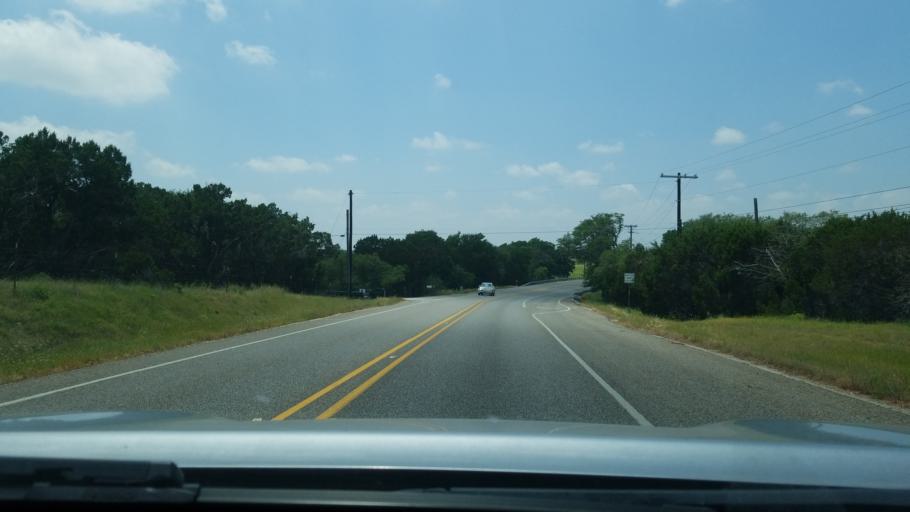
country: US
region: Texas
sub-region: Hays County
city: Woodcreek
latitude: 30.0186
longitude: -98.1415
